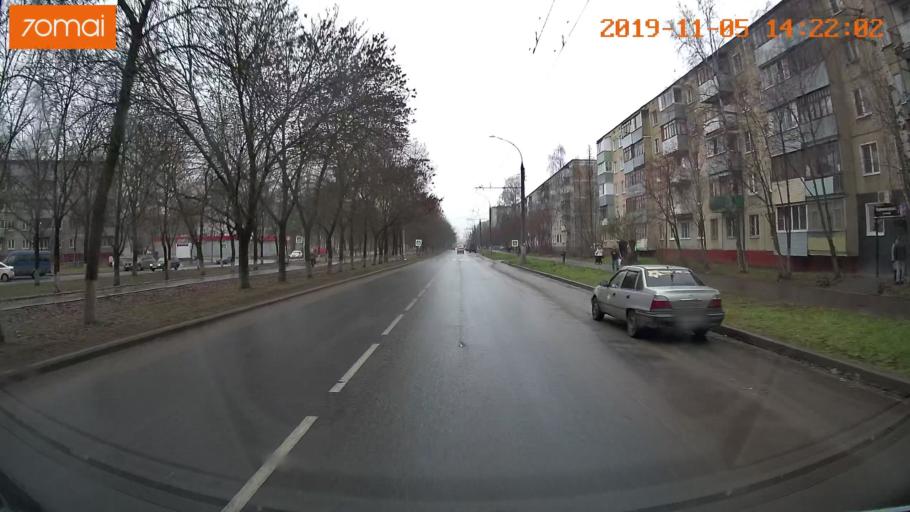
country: RU
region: Ivanovo
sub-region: Gorod Ivanovo
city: Ivanovo
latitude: 56.9615
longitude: 41.0074
